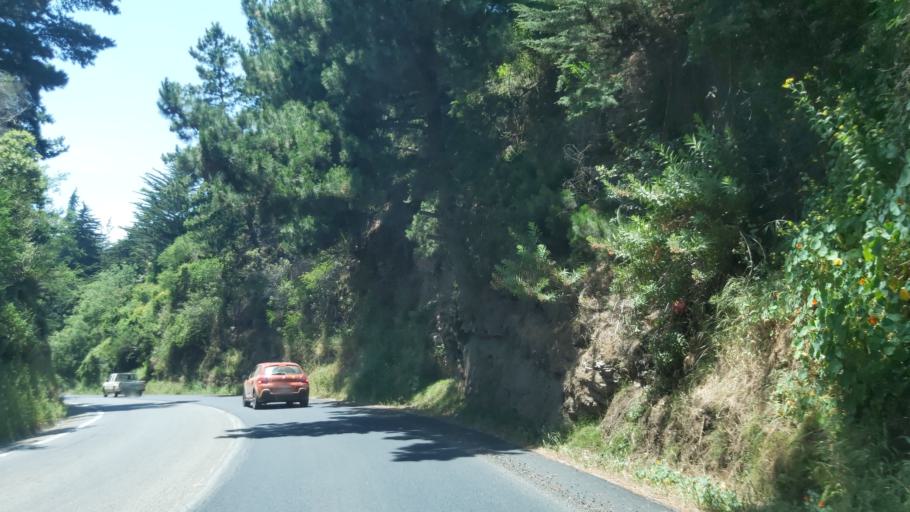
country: CL
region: Maule
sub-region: Provincia de Cauquenes
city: Cauquenes
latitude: -35.8237
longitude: -72.6020
